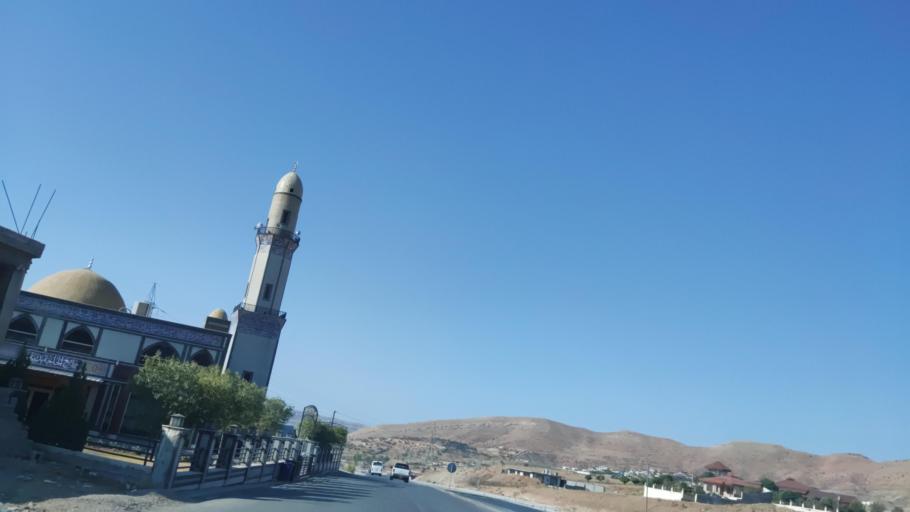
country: IQ
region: Arbil
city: Shaqlawah
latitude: 36.4278
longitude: 44.2695
